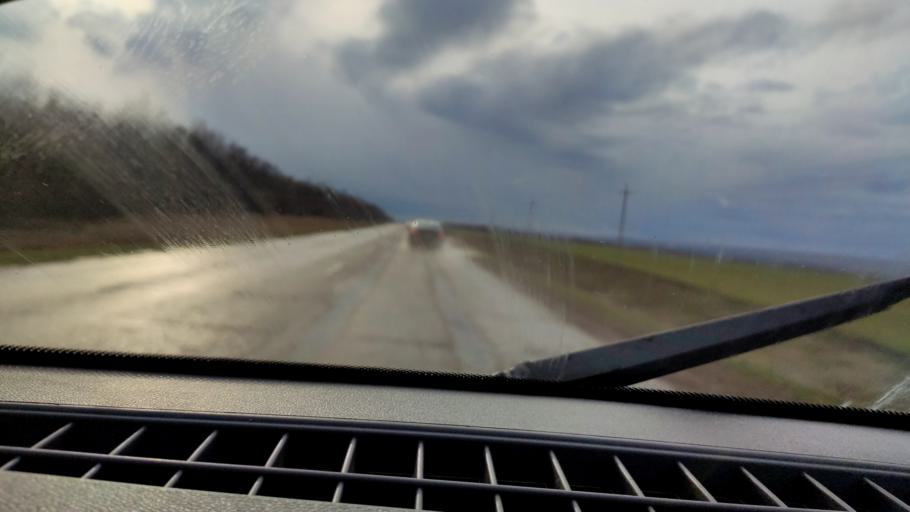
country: RU
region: Bashkortostan
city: Chekmagush
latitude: 55.1062
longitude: 54.9961
